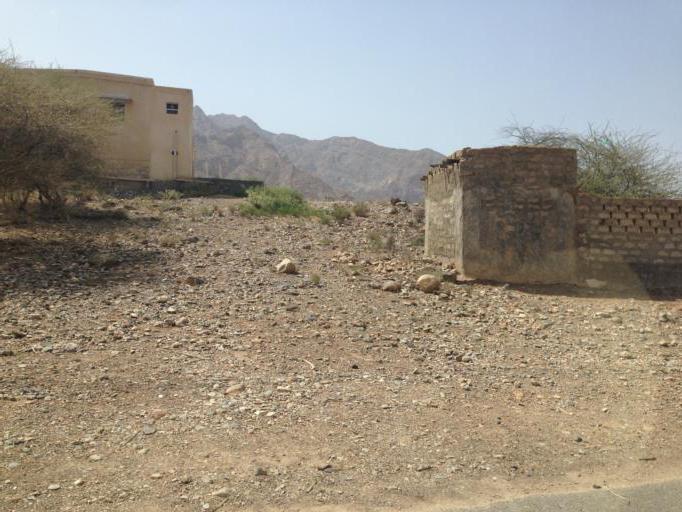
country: OM
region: Ash Sharqiyah
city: Ibra'
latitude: 23.0901
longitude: 58.8559
